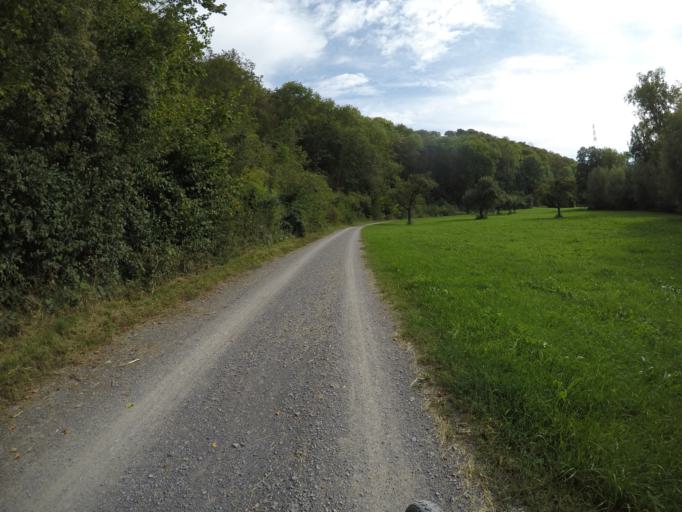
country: DE
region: Baden-Wuerttemberg
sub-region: Regierungsbezirk Stuttgart
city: Eberdingen
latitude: 48.9024
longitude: 8.9799
